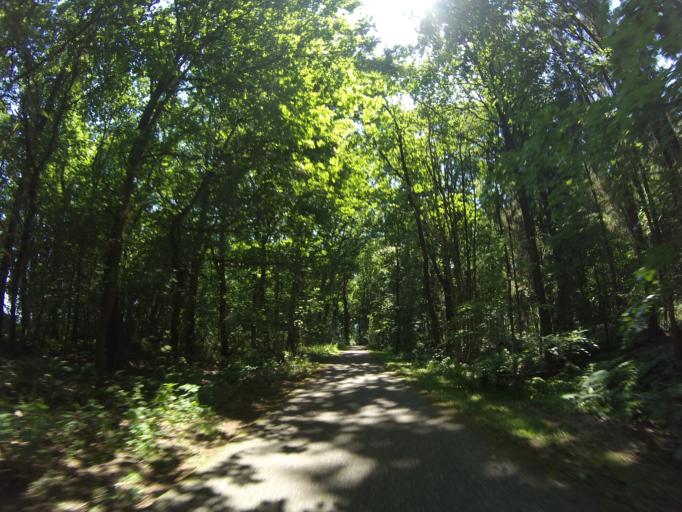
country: NL
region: Drenthe
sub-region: Gemeente Emmen
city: Schoonebeek
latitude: 52.7066
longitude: 6.8301
